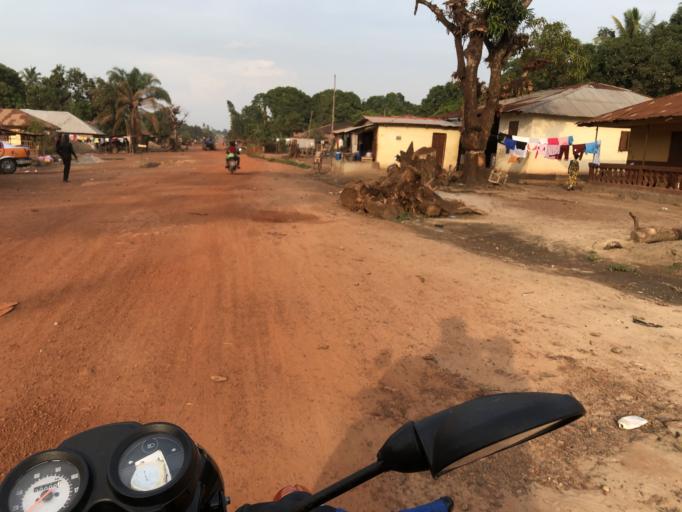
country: SL
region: Northern Province
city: Yonibana
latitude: 8.4667
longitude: -12.2112
